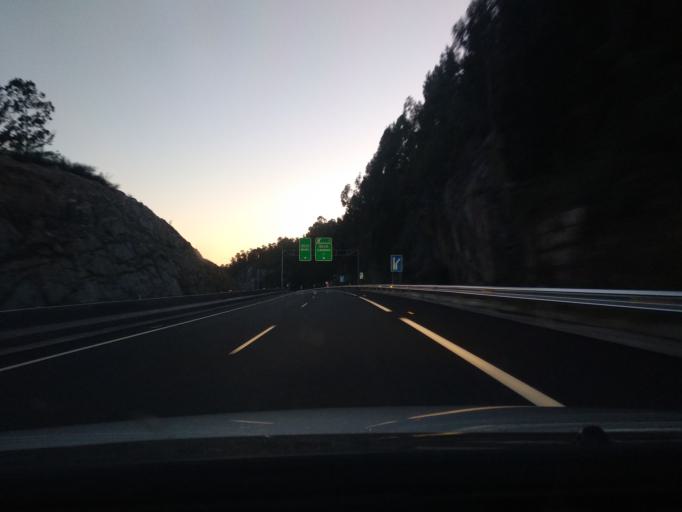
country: ES
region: Galicia
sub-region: Provincia de Pontevedra
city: Moana
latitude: 42.2950
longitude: -8.7509
